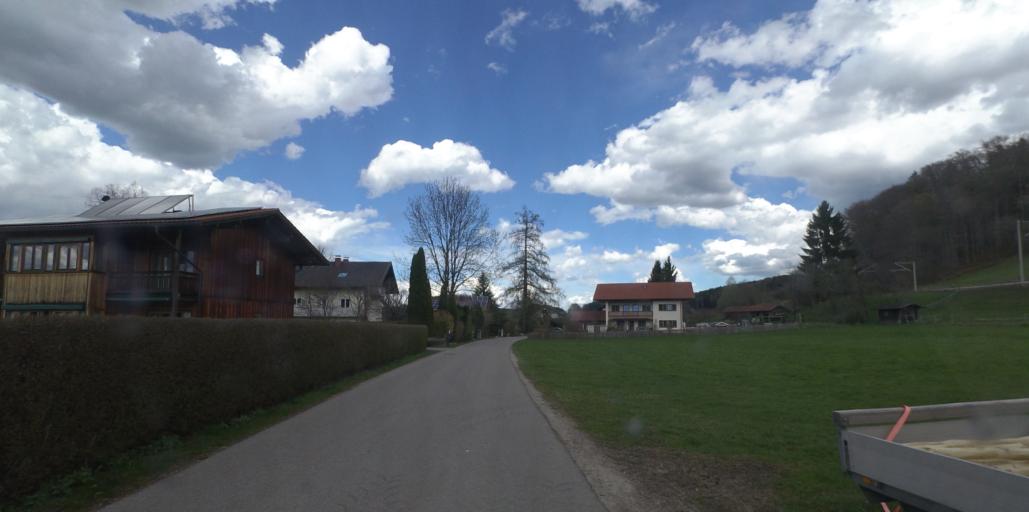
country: DE
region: Bavaria
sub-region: Upper Bavaria
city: Vachendorf
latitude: 47.8372
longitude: 12.6053
